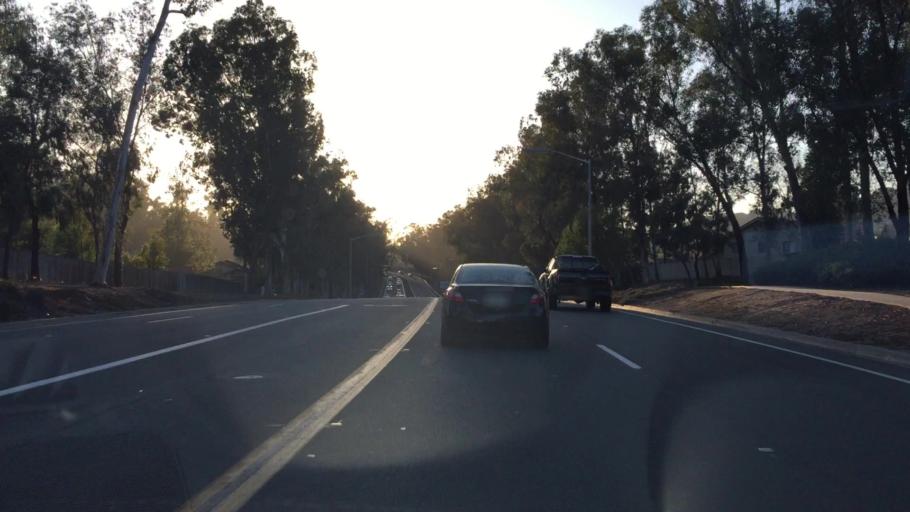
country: US
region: California
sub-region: San Diego County
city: Poway
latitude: 32.9756
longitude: -117.0448
